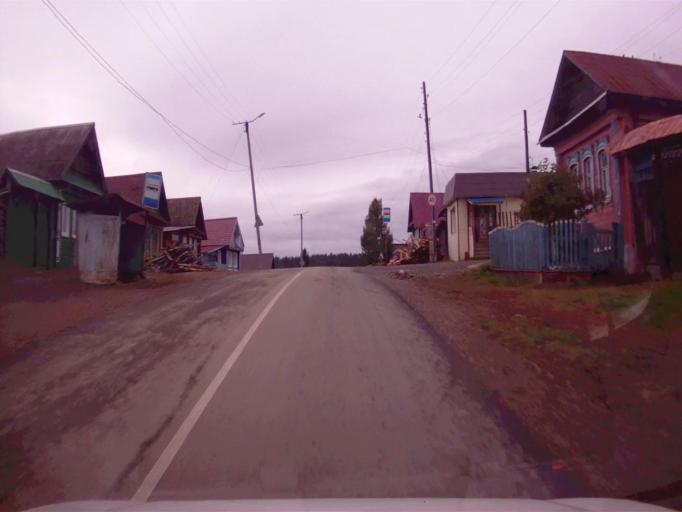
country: RU
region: Chelyabinsk
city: Nyazepetrovsk
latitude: 56.0622
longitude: 59.5752
